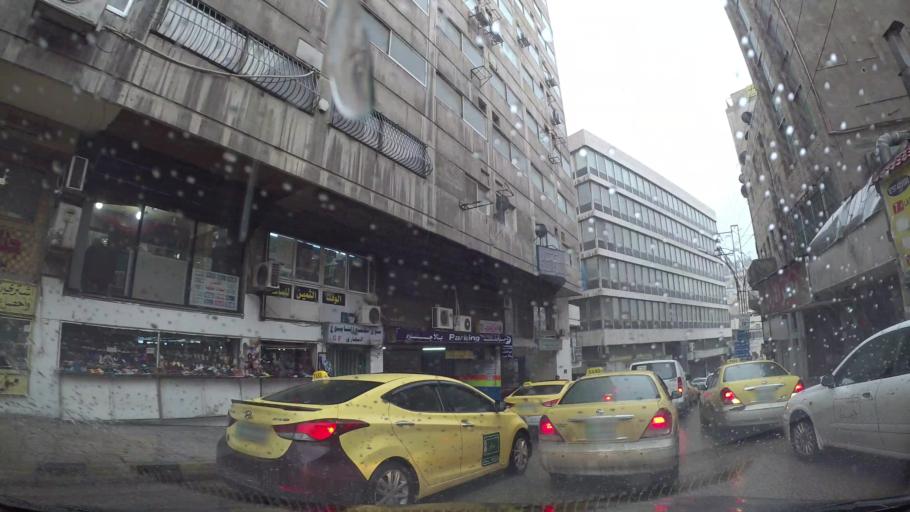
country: JO
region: Amman
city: Amman
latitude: 31.9519
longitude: 35.9351
